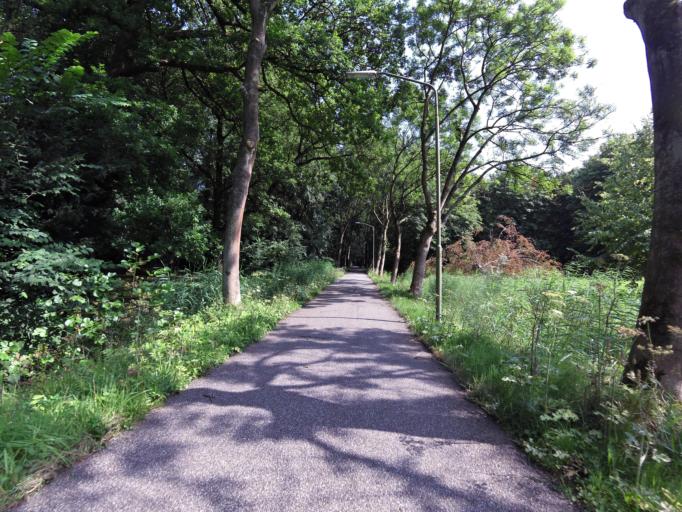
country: NL
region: South Holland
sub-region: Gemeente Dordrecht
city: Dordrecht
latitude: 51.7942
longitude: 4.6862
